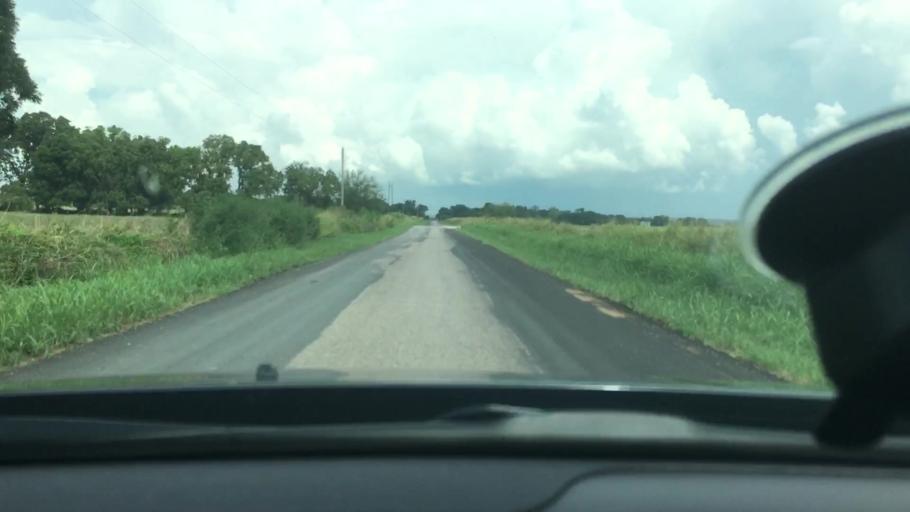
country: US
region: Oklahoma
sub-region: Carter County
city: Dickson
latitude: 34.2072
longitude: -96.8982
